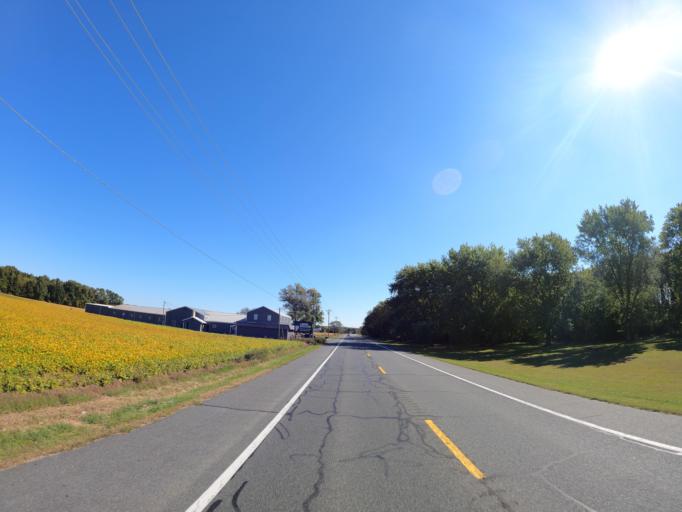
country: US
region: Delaware
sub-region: Sussex County
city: Bridgeville
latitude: 38.8054
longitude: -75.5301
